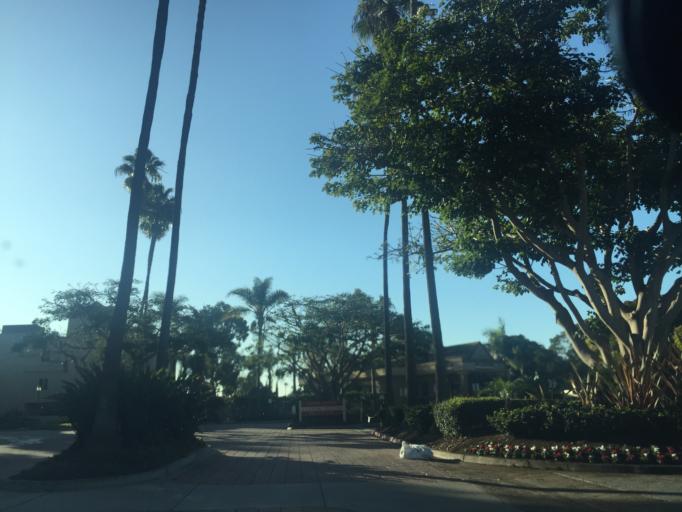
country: US
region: California
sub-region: San Diego County
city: La Jolla
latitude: 32.8679
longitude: -117.2272
